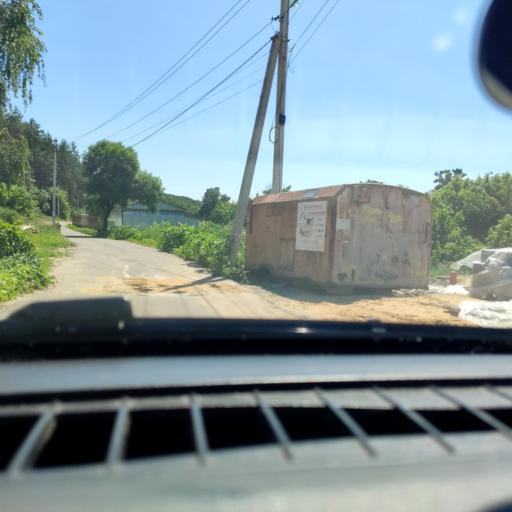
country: RU
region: Voronezj
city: Podgornoye
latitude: 51.7921
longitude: 39.1352
